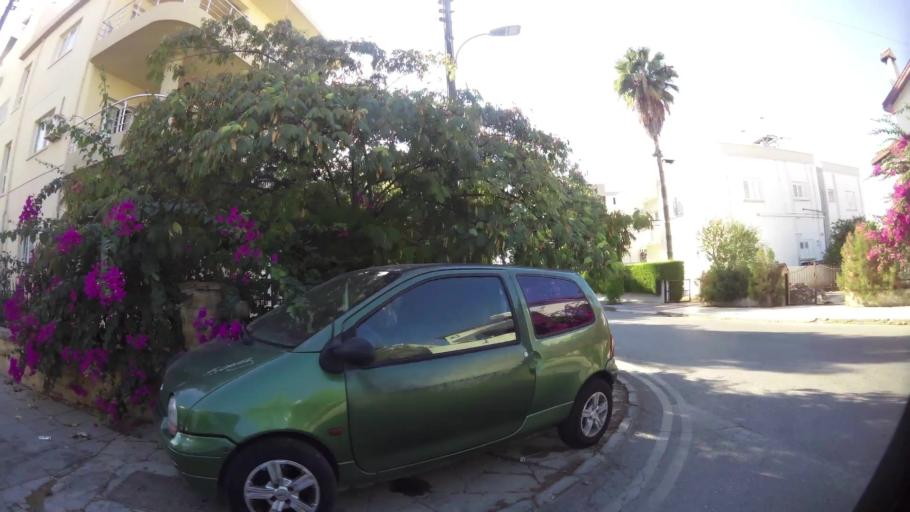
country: CY
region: Lefkosia
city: Nicosia
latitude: 35.1972
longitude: 33.3389
